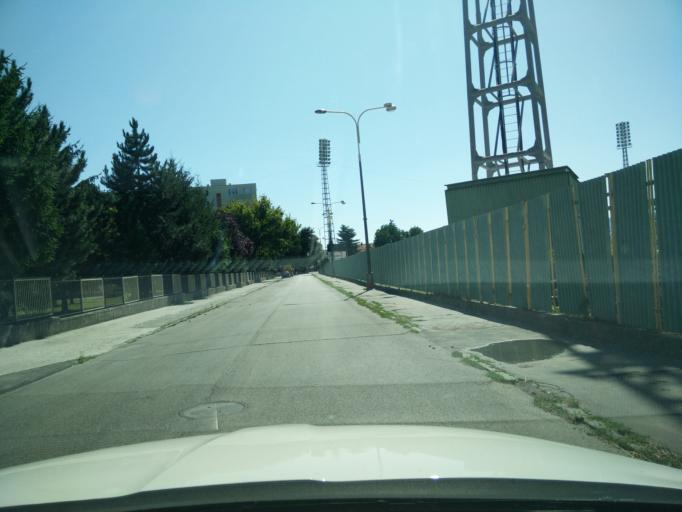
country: SK
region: Nitriansky
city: Prievidza
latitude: 48.7790
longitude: 18.6253
